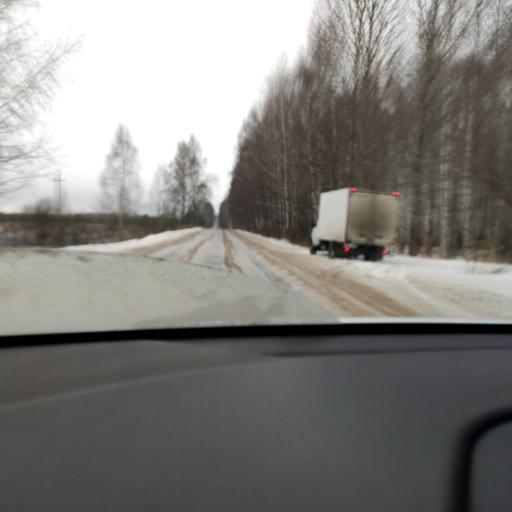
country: RU
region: Tatarstan
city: Osinovo
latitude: 55.8833
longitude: 48.8204
